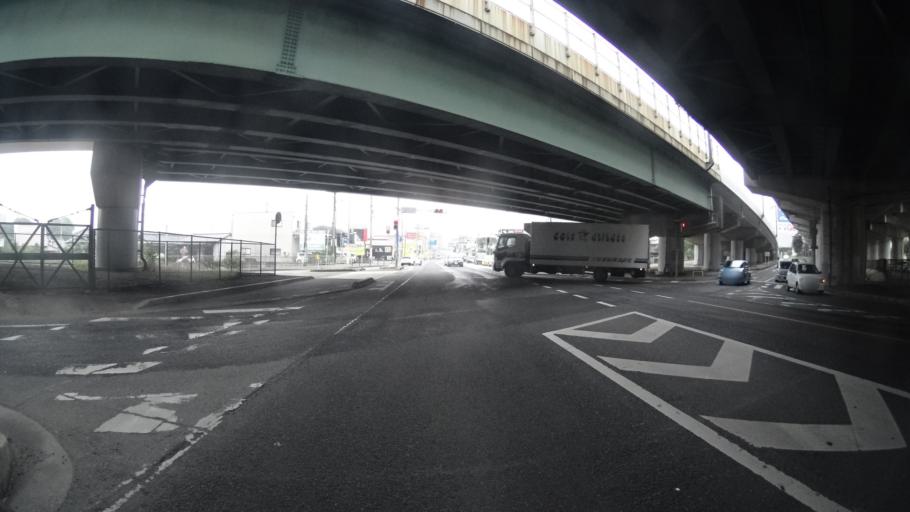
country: JP
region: Fukuoka
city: Onojo
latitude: 33.5245
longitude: 130.4954
